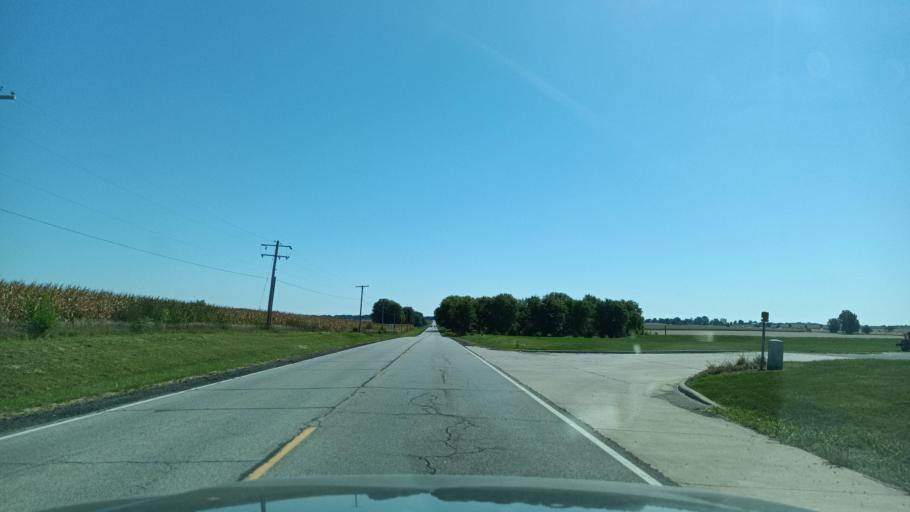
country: US
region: Illinois
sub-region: Peoria County
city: Elmwood
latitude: 40.8301
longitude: -89.8680
